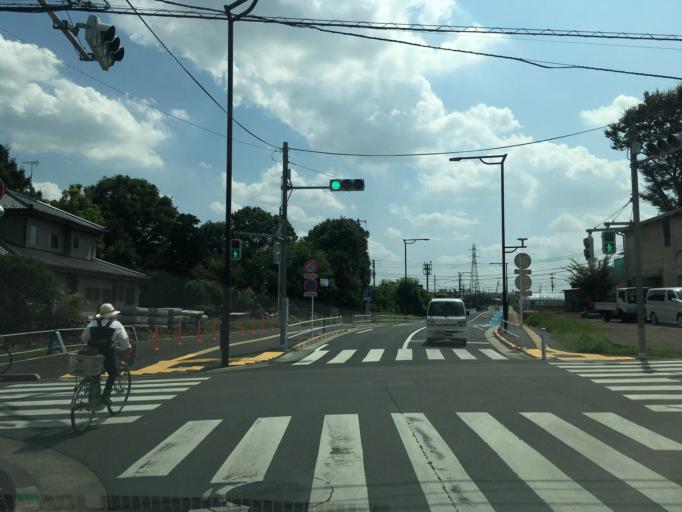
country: JP
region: Tokyo
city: Higashimurayama-shi
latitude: 35.7673
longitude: 139.4853
